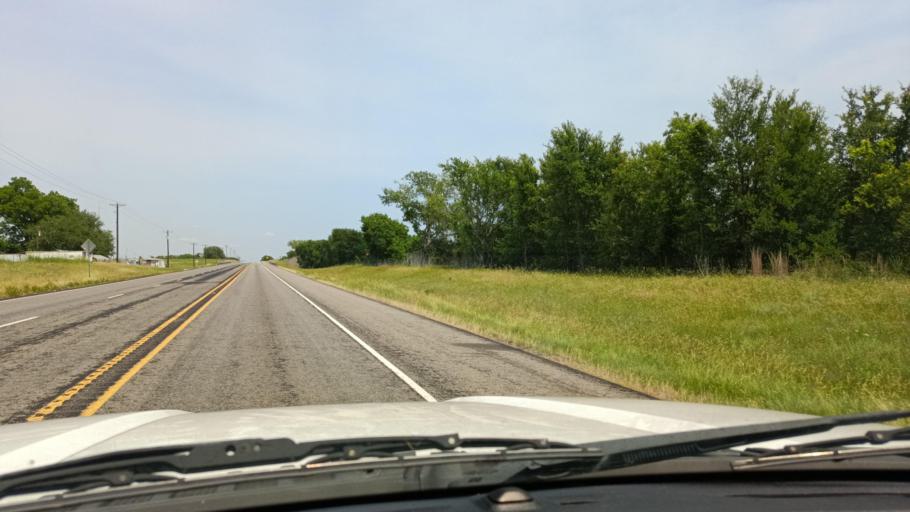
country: US
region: Texas
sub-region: Milam County
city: Cameron
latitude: 30.8488
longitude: -97.0586
